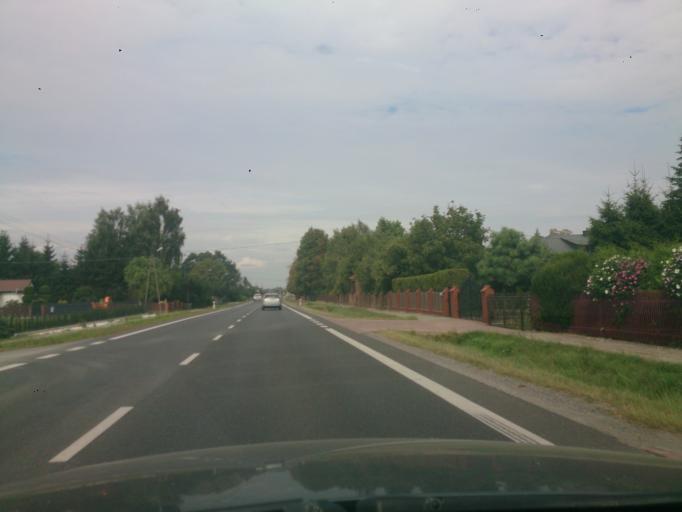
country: PL
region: Subcarpathian Voivodeship
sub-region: Powiat kolbuszowski
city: Kolbuszowa
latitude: 50.2284
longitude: 21.7917
